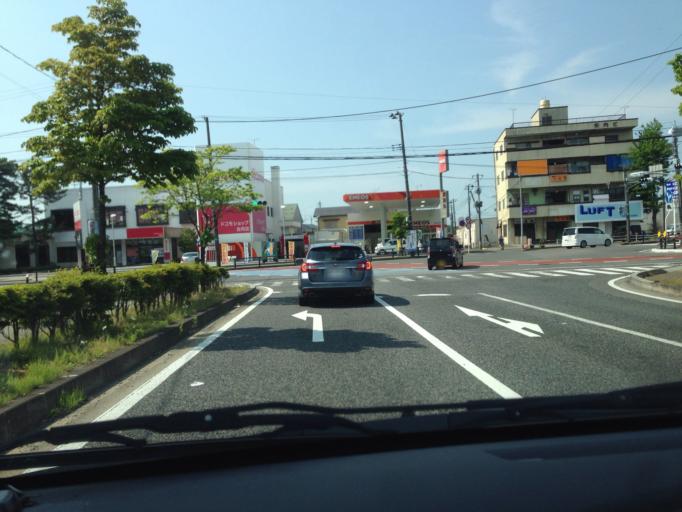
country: JP
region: Tochigi
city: Kuroiso
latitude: 37.1306
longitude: 140.2012
